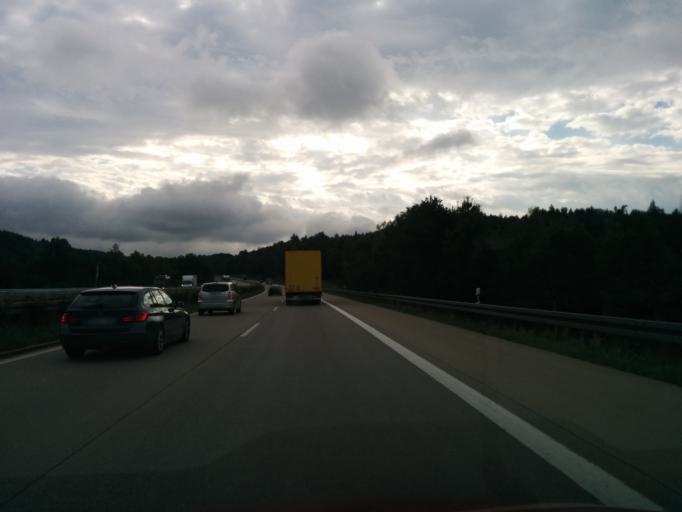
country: DE
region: Bavaria
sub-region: Lower Bavaria
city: Bogen
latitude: 48.9343
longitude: 12.6771
